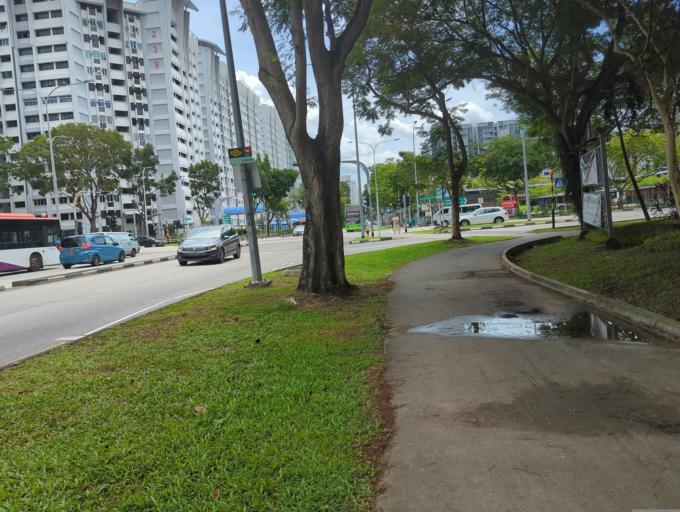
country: MY
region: Johor
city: Kampung Pasir Gudang Baru
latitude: 1.3924
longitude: 103.8980
